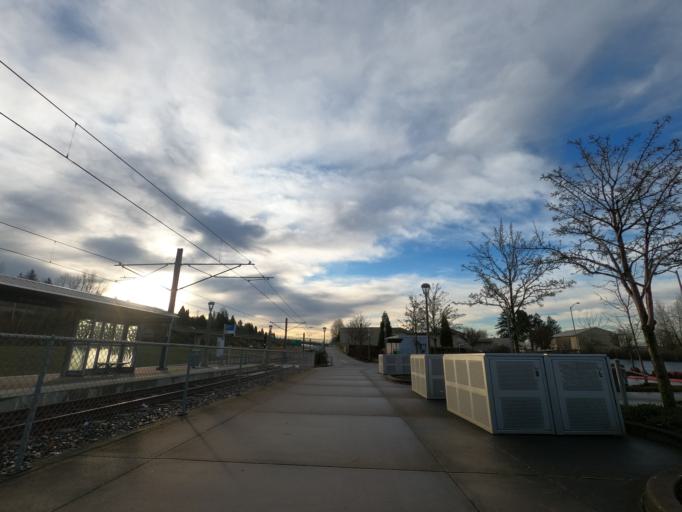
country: US
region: Oregon
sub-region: Multnomah County
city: Lents
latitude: 45.4534
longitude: -122.5737
